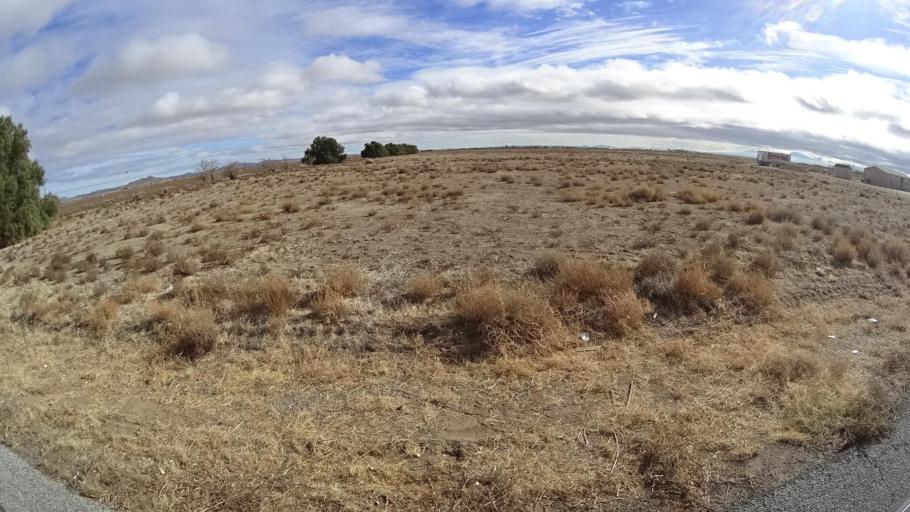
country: US
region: California
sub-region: Kern County
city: Rosamond
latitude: 34.8269
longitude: -118.3087
